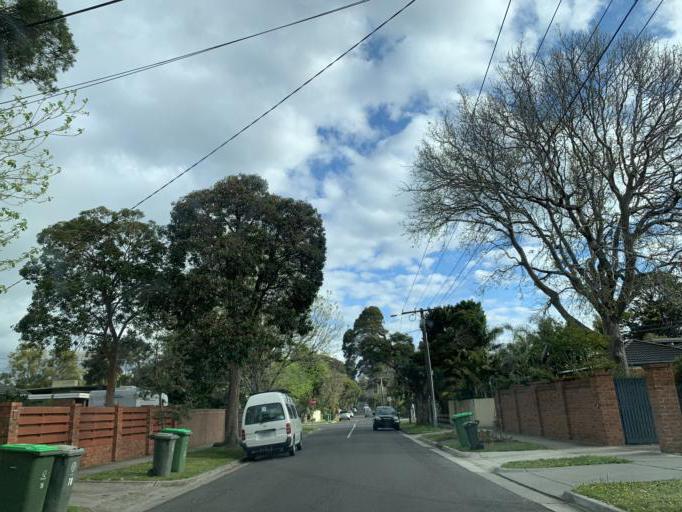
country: AU
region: Victoria
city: Beaumaris
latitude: -37.9845
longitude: 145.0403
